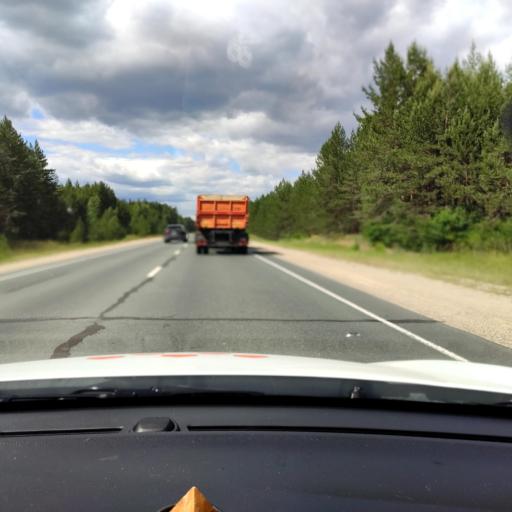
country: RU
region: Mariy-El
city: Krasnogorskiy
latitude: 56.0847
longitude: 48.3532
